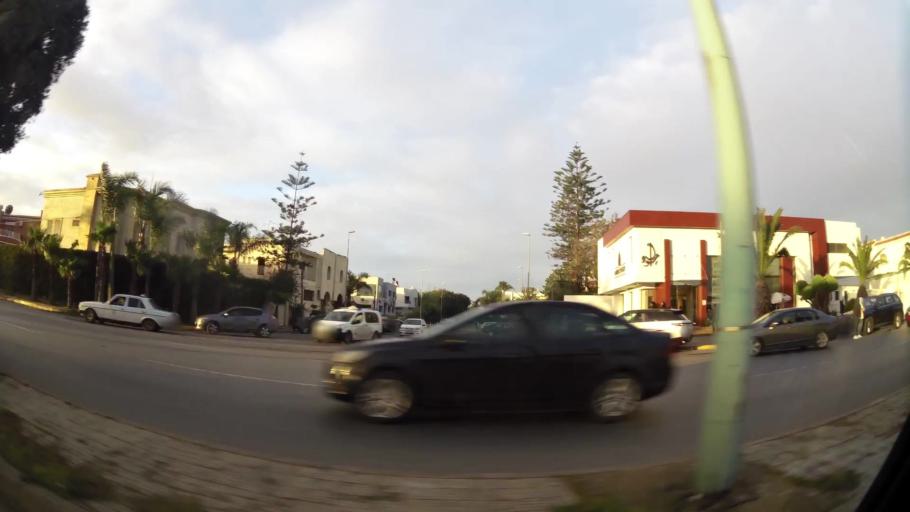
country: MA
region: Grand Casablanca
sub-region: Casablanca
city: Casablanca
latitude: 33.5682
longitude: -7.6597
